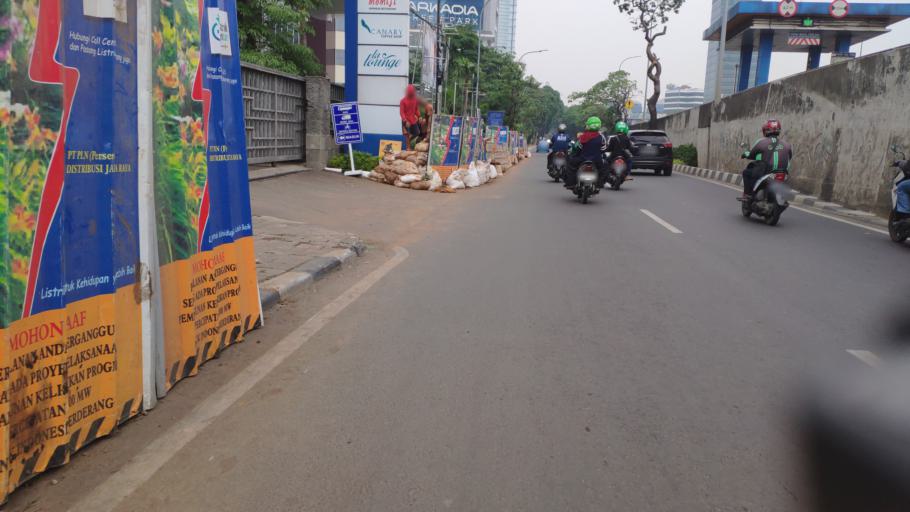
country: ID
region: Jakarta Raya
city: Jakarta
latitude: -6.3013
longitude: 106.8353
